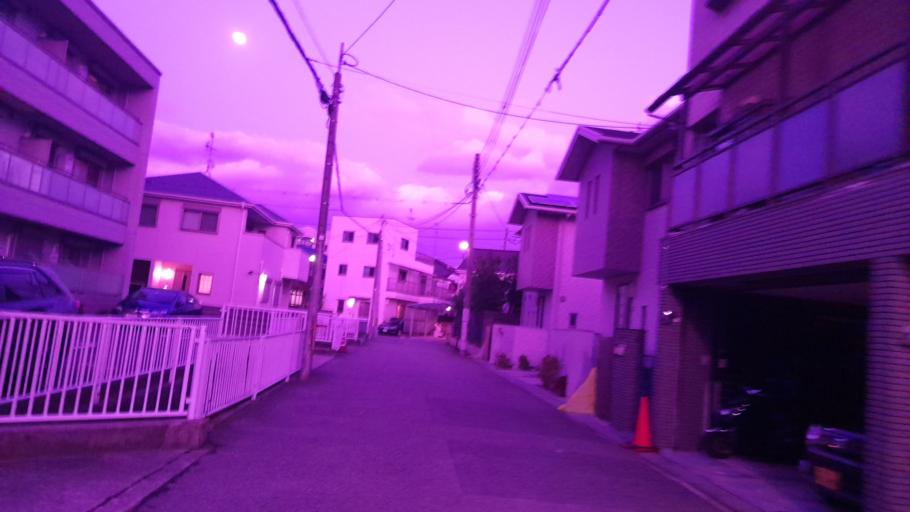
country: JP
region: Hyogo
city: Amagasaki
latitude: 34.7487
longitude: 135.4422
